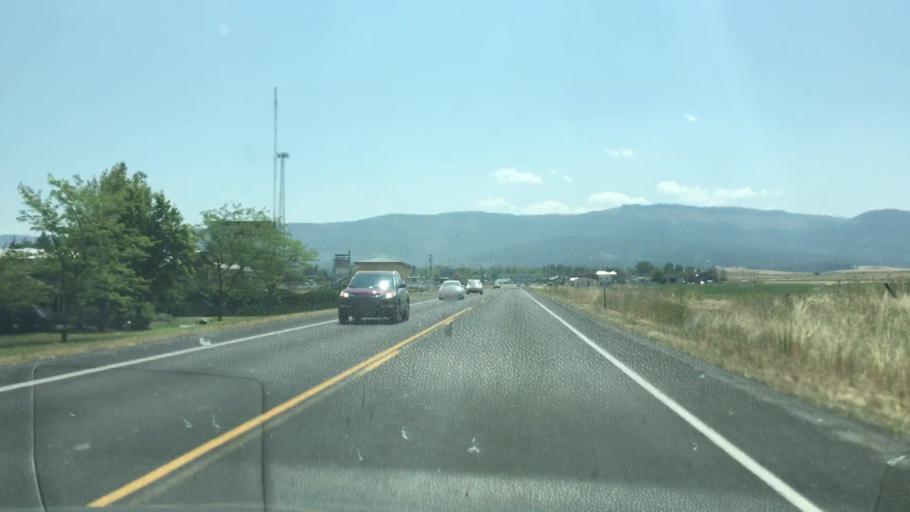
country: US
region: Idaho
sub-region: Idaho County
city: Grangeville
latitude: 45.9326
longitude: -116.1326
